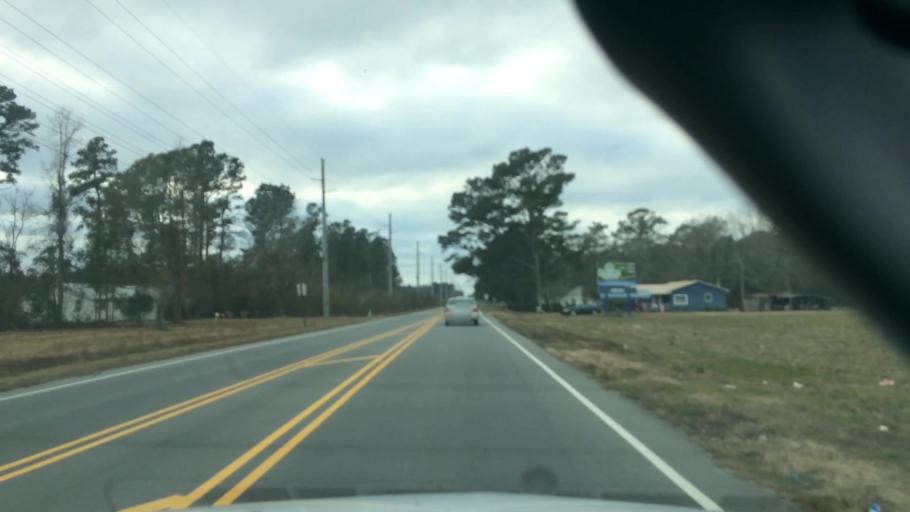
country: US
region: North Carolina
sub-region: Brunswick County
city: Carolina Shores
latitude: 33.9364
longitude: -78.5710
